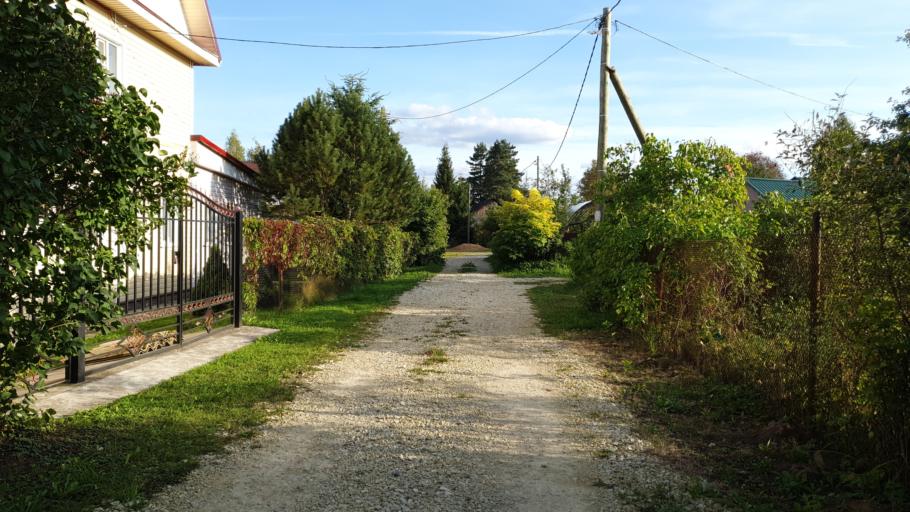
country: RU
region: Leningrad
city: Ivangorod
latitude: 59.4301
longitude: 28.3212
